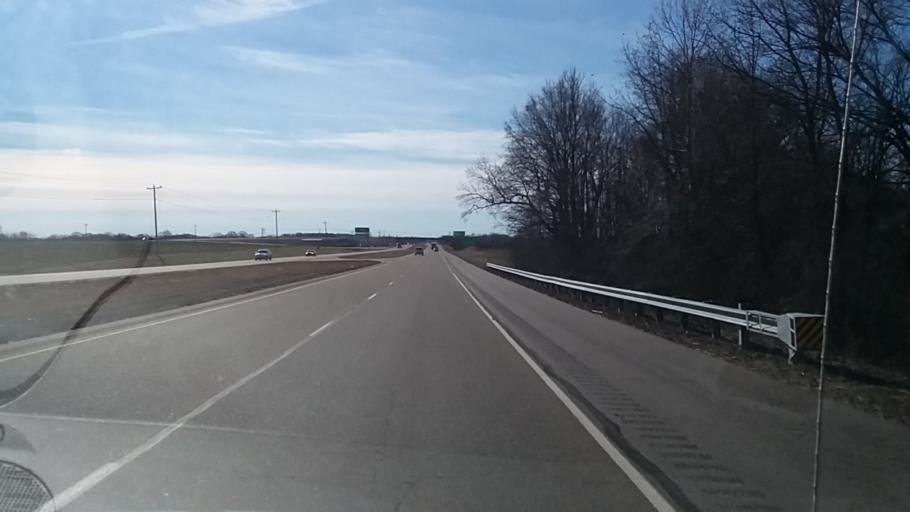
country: US
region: Tennessee
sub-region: Crockett County
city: Alamo
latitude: 35.8893
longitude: -89.2343
